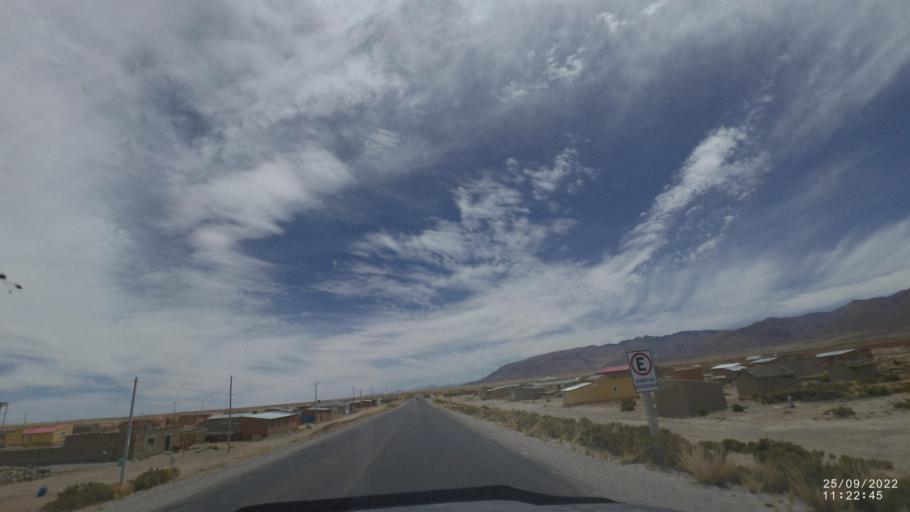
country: BO
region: Oruro
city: Challapata
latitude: -19.1208
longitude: -66.7692
